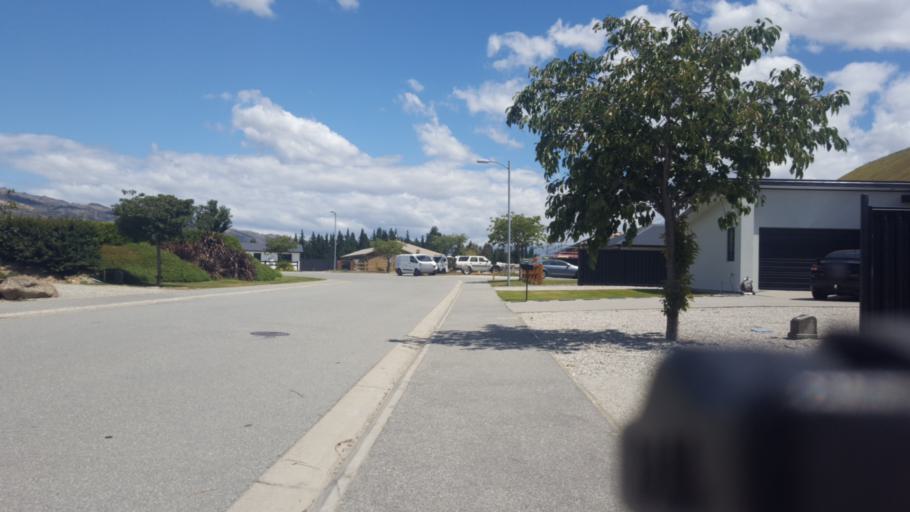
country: NZ
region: Otago
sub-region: Queenstown-Lakes District
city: Wanaka
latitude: -44.9811
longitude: 169.2350
